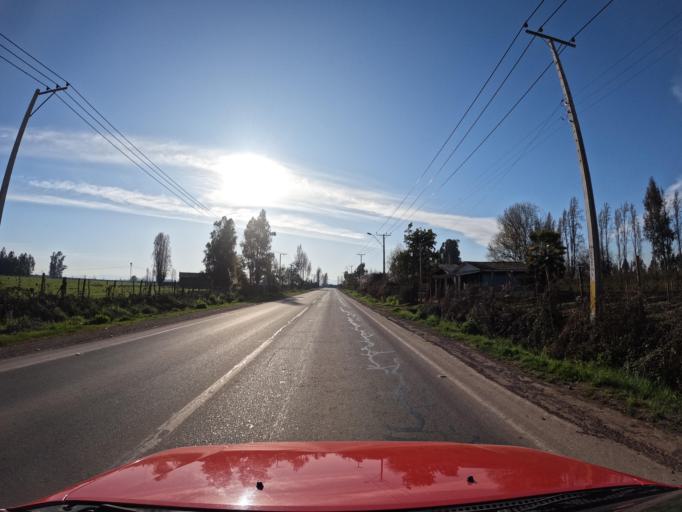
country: CL
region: Maule
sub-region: Provincia de Curico
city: Teno
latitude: -34.9043
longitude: -71.0527
